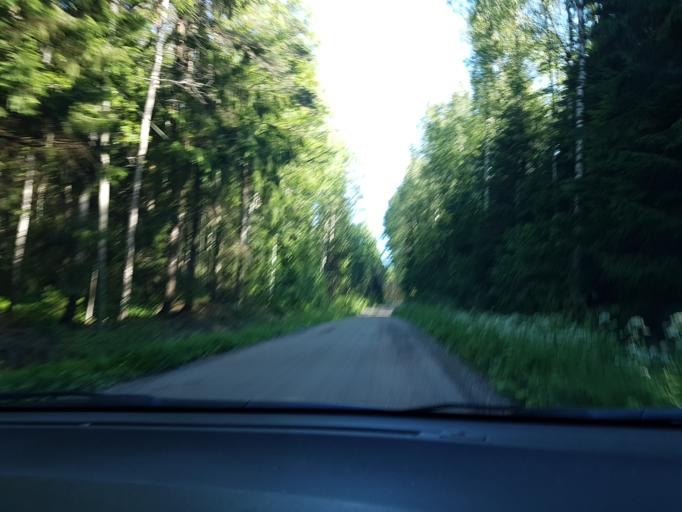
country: FI
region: Uusimaa
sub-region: Helsinki
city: Sibbo
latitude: 60.2685
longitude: 25.2293
